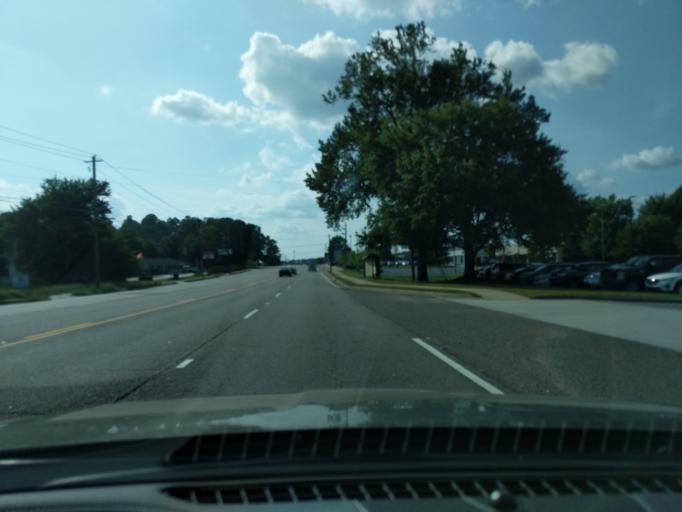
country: US
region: Georgia
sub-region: Columbia County
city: Martinez
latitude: 33.5148
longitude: -82.0616
